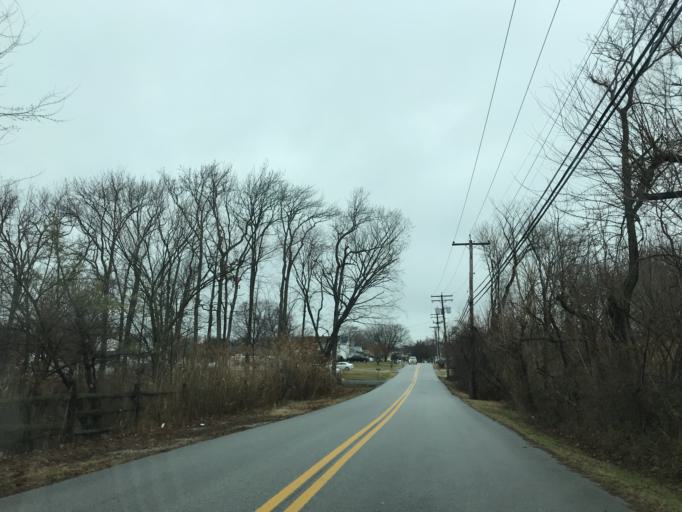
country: US
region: Maryland
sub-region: Baltimore County
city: Edgemere
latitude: 39.2241
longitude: -76.4454
